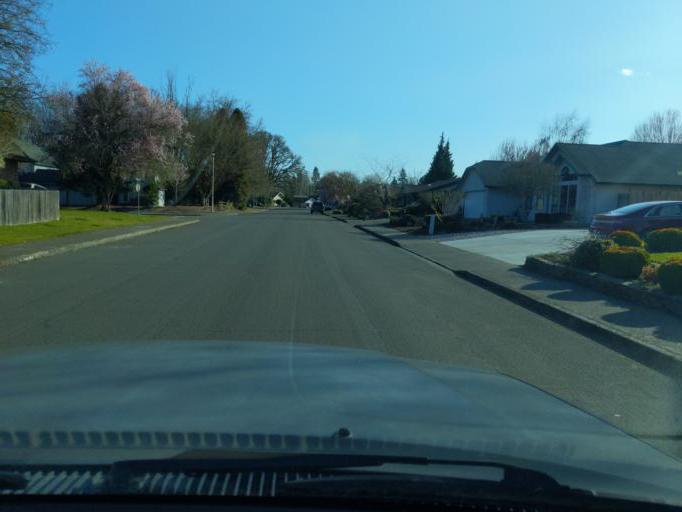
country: US
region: Oregon
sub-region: Yamhill County
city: McMinnville
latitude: 45.1986
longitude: -123.2141
